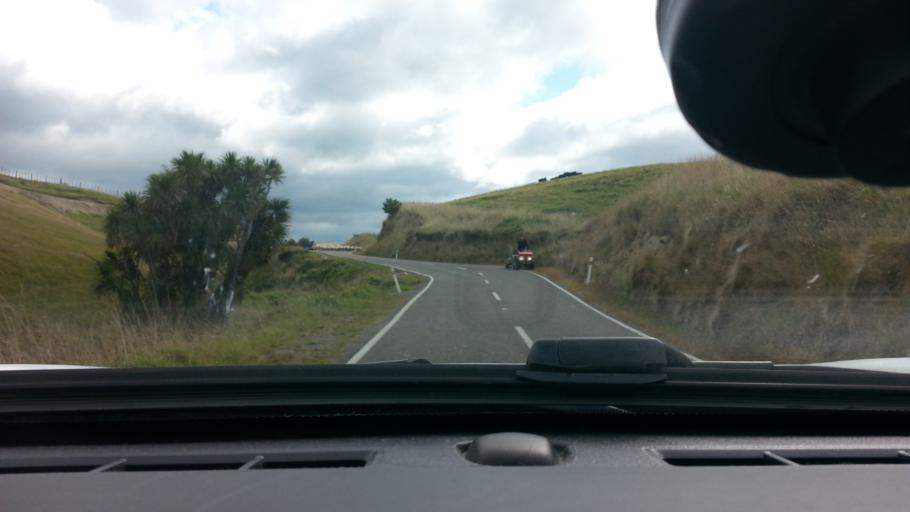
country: NZ
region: Wellington
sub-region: Upper Hutt City
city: Upper Hutt
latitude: -41.3999
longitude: 175.1768
